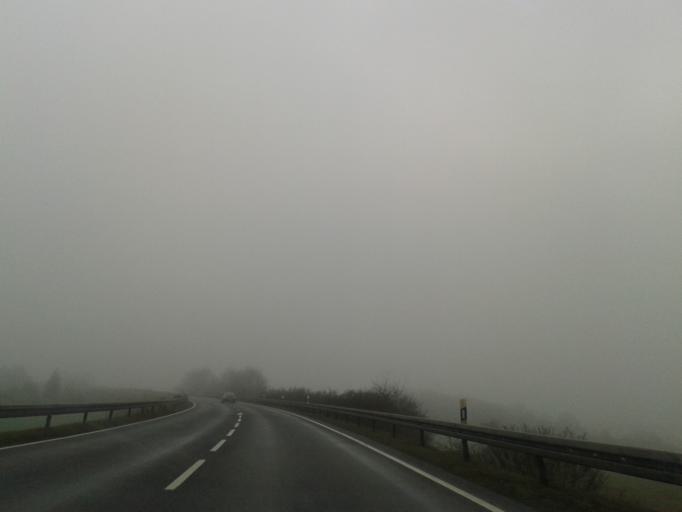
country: DE
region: Bavaria
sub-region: Upper Franconia
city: Sesslach
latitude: 50.2162
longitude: 10.8310
